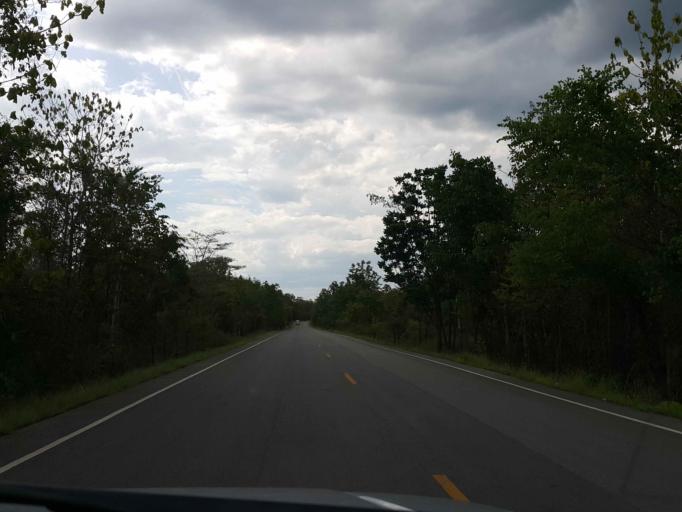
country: TH
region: Sukhothai
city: Thung Saliam
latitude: 17.3745
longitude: 99.4032
